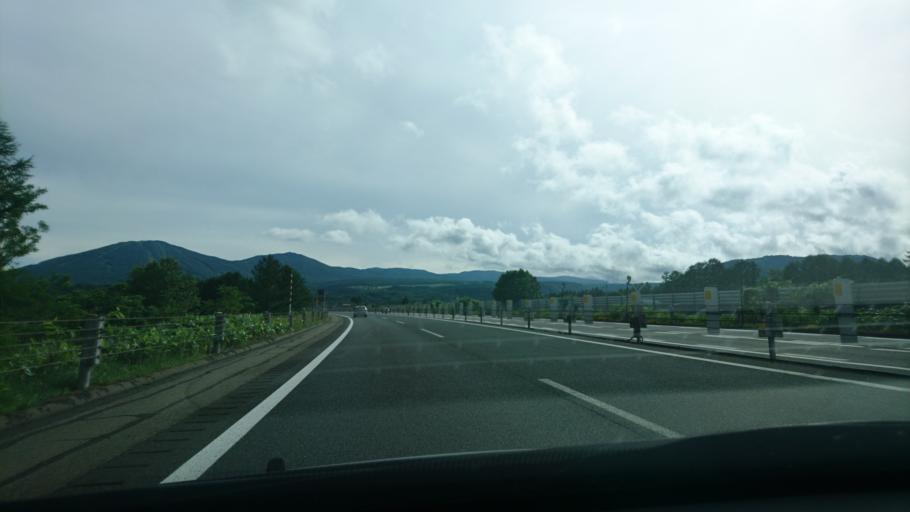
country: JP
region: Akita
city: Hanawa
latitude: 40.0328
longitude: 140.9860
